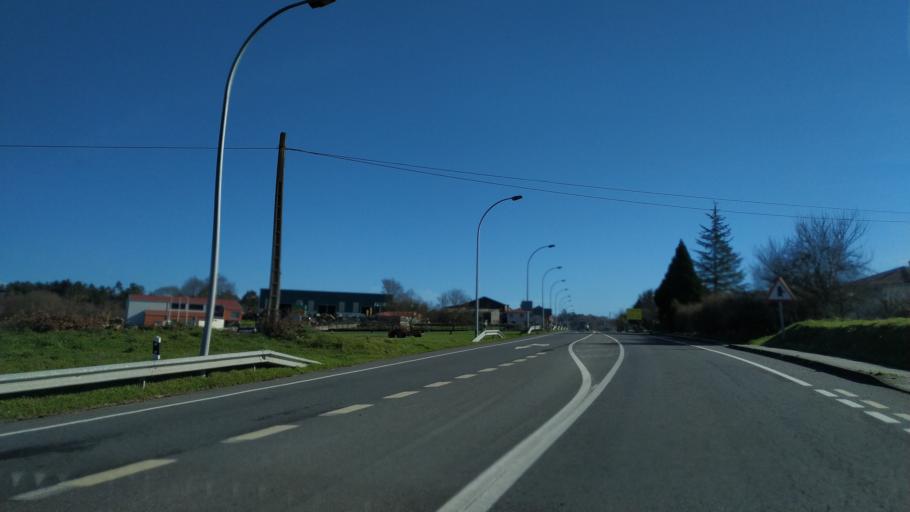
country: ES
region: Galicia
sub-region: Provincia de Pontevedra
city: Silleda
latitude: 42.6834
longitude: -8.1950
